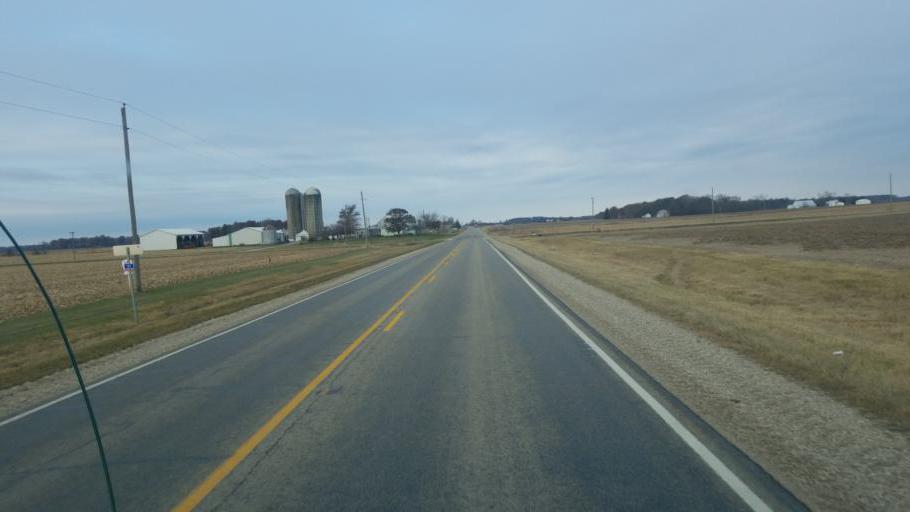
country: US
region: Indiana
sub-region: Adams County
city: Geneva
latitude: 40.5425
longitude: -84.8463
